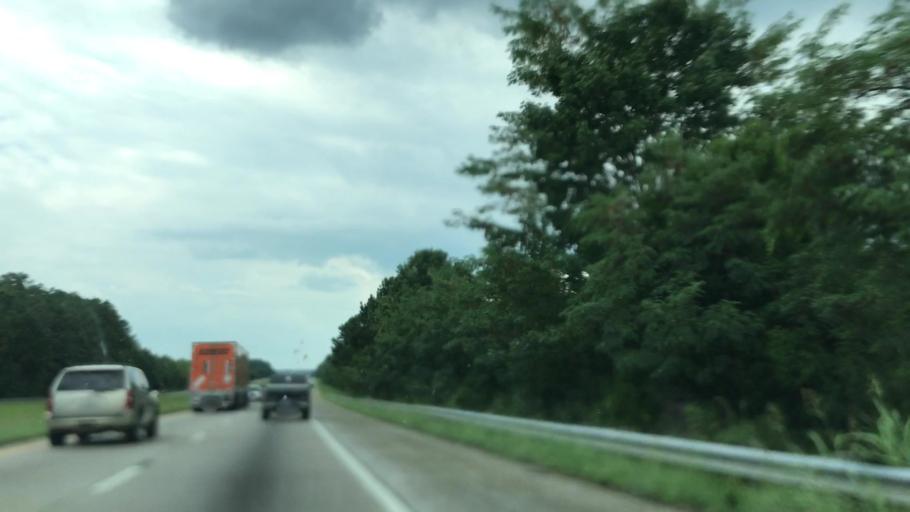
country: US
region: South Carolina
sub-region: Fairfield County
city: Winnsboro Mills
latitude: 34.3558
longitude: -80.9984
